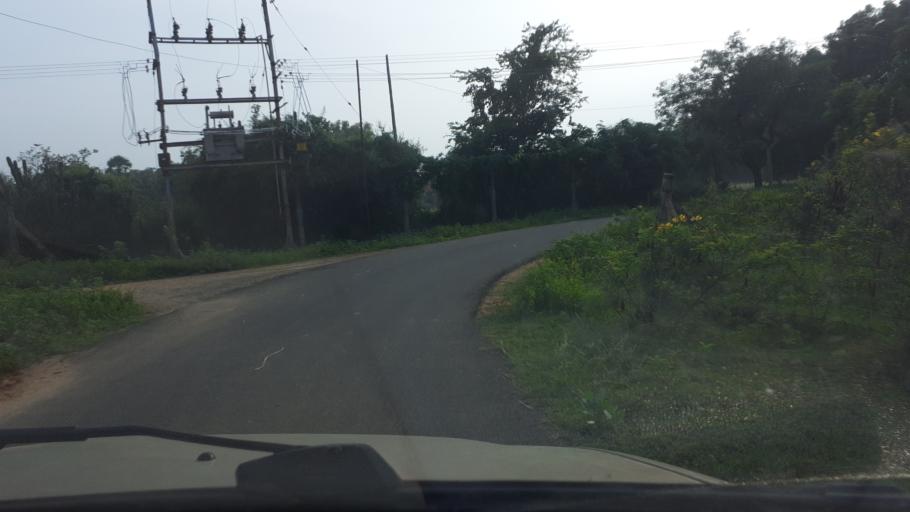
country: IN
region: Tamil Nadu
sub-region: Tirunelveli Kattabo
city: Kalakkadu
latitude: 8.4682
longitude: 77.5848
